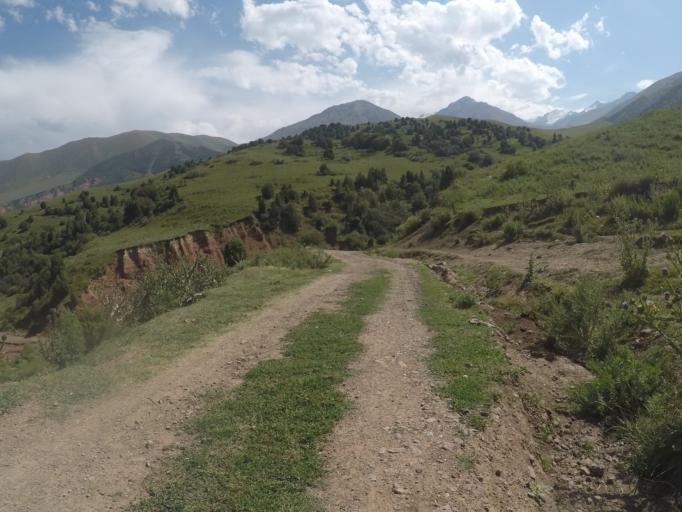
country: KG
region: Chuy
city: Bishkek
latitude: 42.6436
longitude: 74.6038
